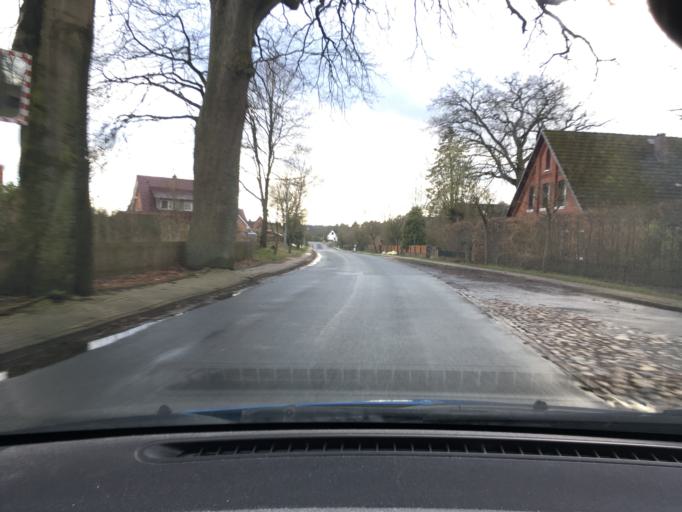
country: DE
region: Lower Saxony
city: Hanstedt
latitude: 53.2358
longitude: 10.0241
